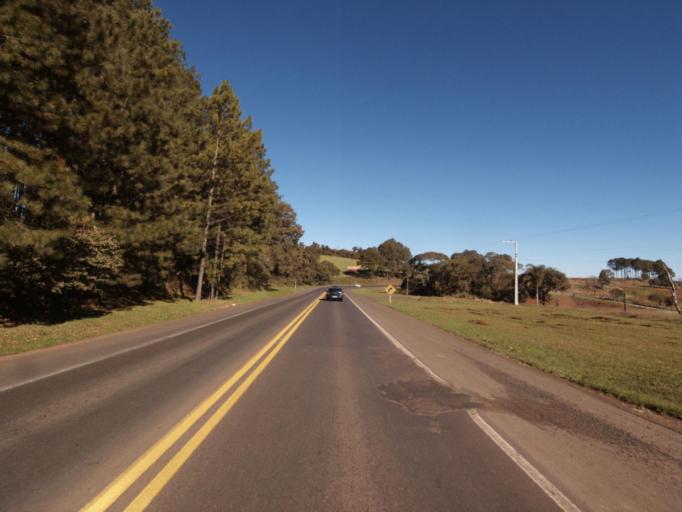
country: BR
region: Santa Catarina
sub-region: Xanxere
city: Xanxere
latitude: -26.9024
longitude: -52.4629
